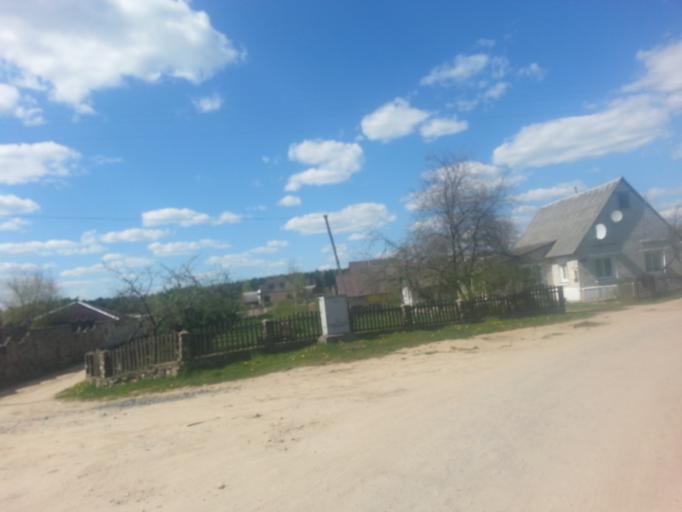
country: BY
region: Minsk
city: Narach
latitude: 54.9407
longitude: 26.6867
